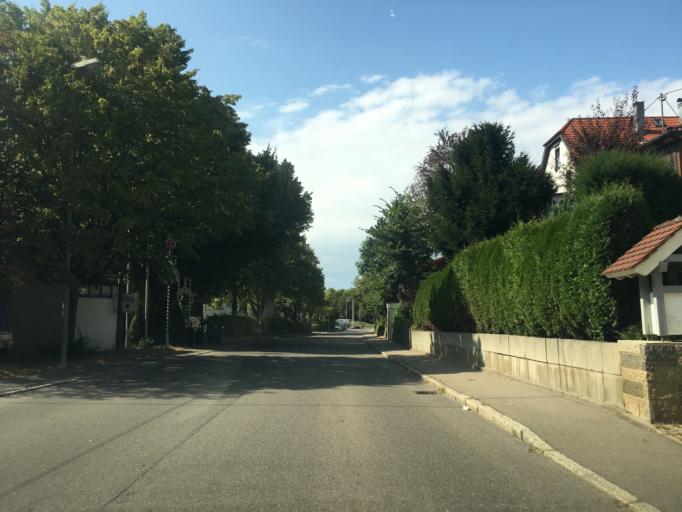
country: DE
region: Baden-Wuerttemberg
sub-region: Tuebingen Region
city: Gomaringen
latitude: 48.4281
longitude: 9.1626
